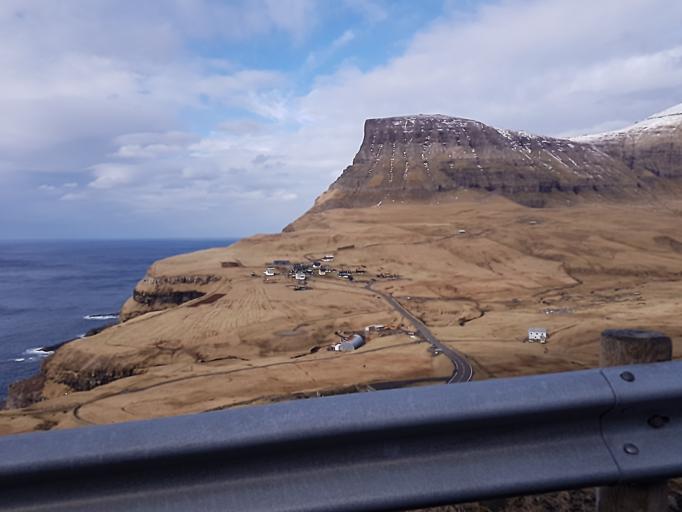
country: FO
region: Vagar
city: Sorvagur
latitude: 62.1061
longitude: -7.4293
